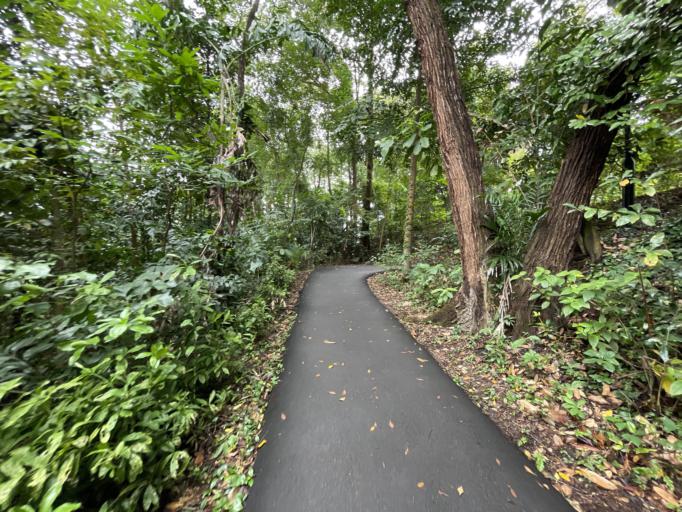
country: SG
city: Singapore
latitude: 1.2773
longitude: 103.8145
